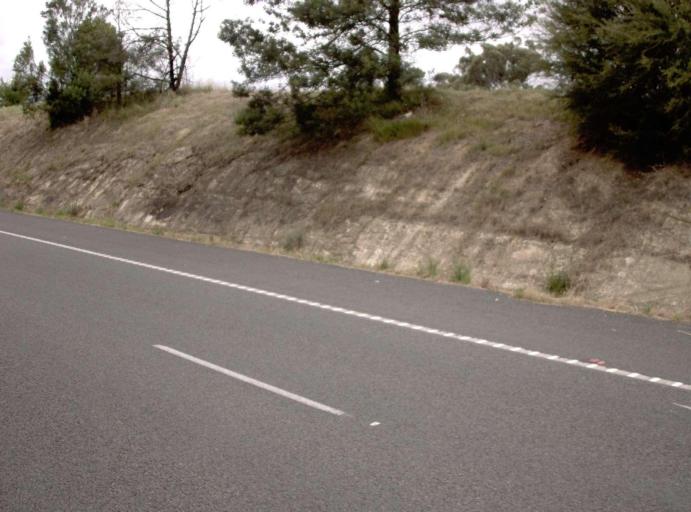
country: AU
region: Victoria
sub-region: Yarra Ranges
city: Badger Creek
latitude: -37.6841
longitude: 145.4841
